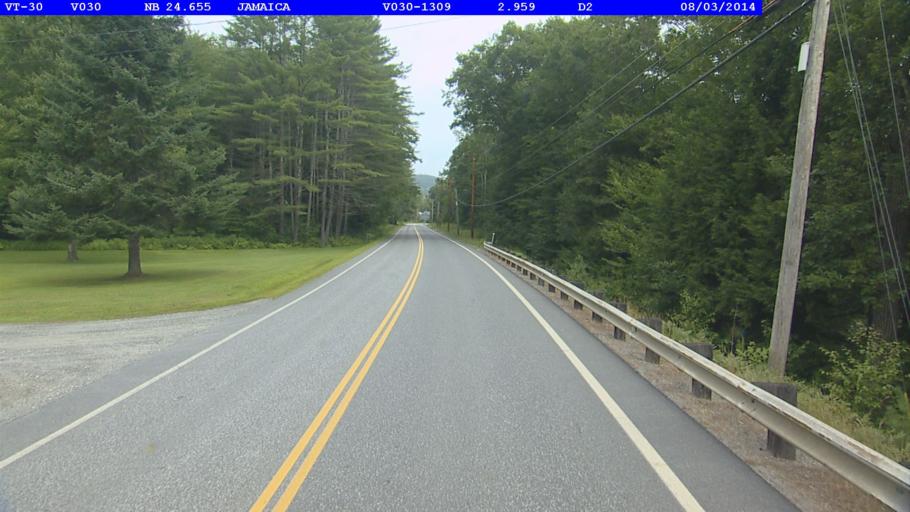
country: US
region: Vermont
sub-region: Windham County
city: Dover
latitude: 43.0927
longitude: -72.7690
